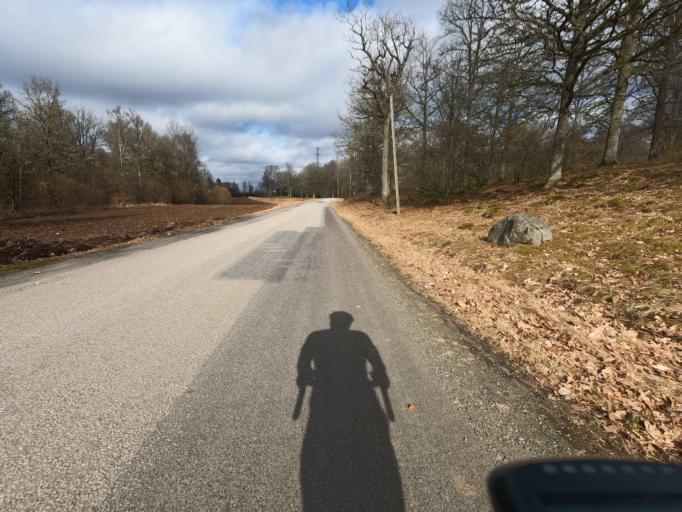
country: SE
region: Kronoberg
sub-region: Alvesta Kommun
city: Vislanda
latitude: 56.8221
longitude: 14.5214
